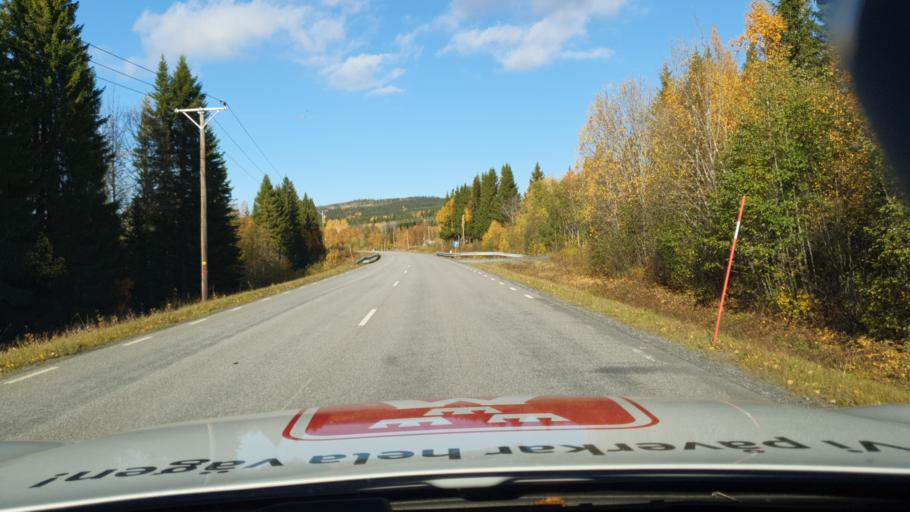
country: SE
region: Jaemtland
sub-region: Are Kommun
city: Jarpen
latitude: 63.3756
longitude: 13.4294
